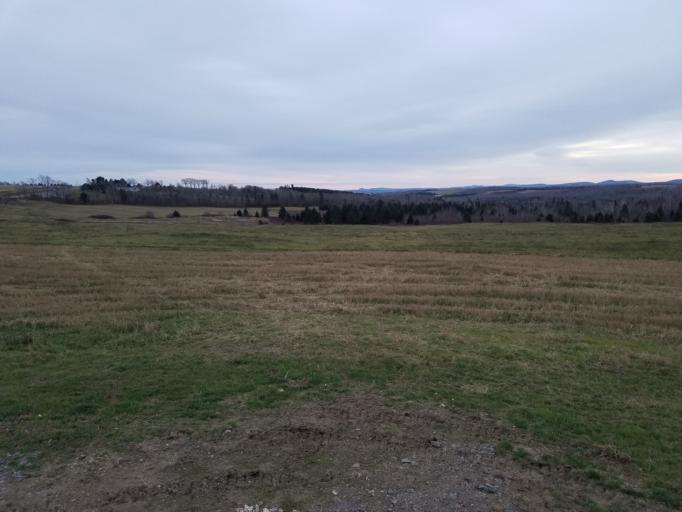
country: US
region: Maine
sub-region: Aroostook County
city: Caribou
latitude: 46.8679
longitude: -68.2082
